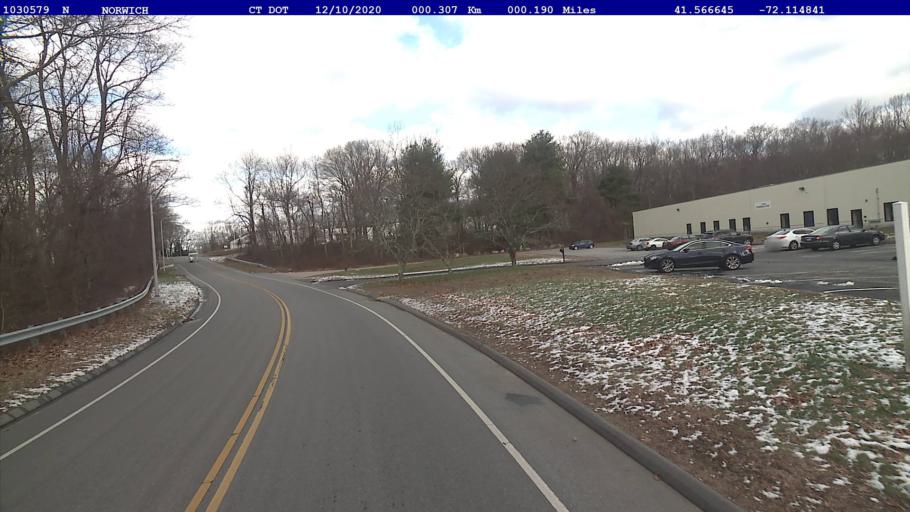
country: US
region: Connecticut
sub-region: New London County
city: Norwich
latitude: 41.5666
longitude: -72.1149
